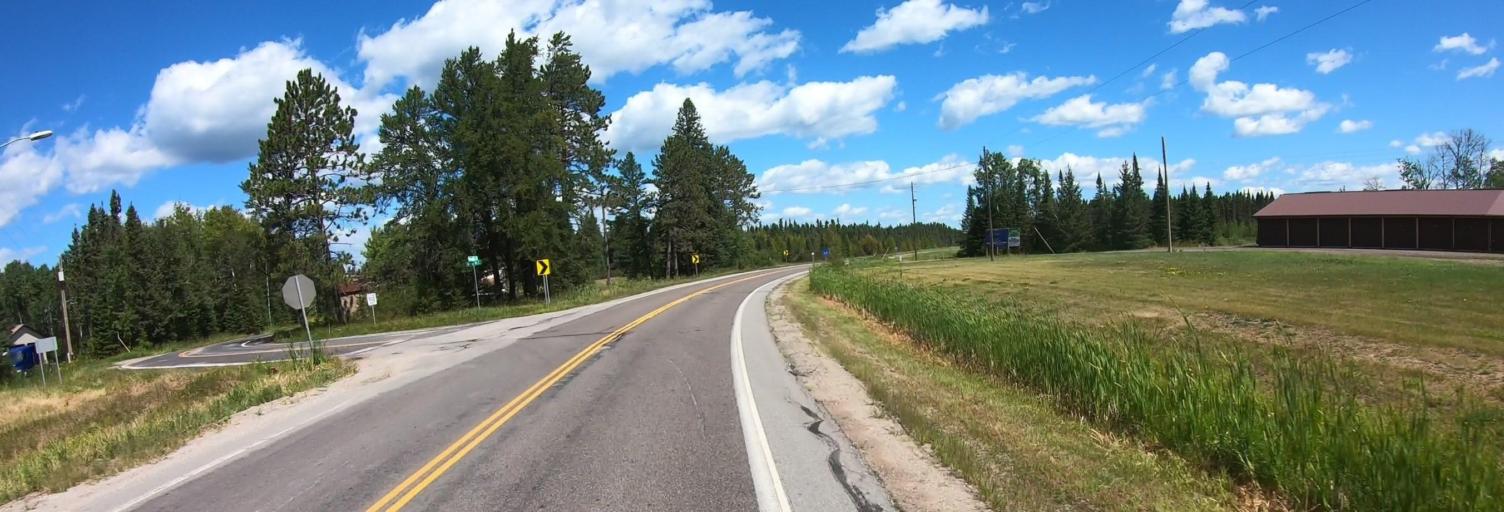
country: US
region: Minnesota
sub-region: Saint Louis County
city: Mountain Iron
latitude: 47.8700
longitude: -92.6855
